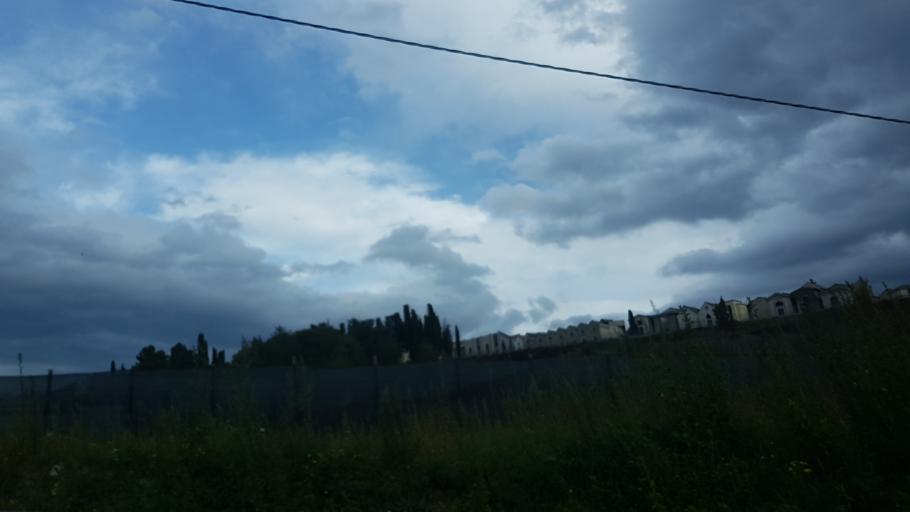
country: IT
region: Abruzzo
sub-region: Provincia dell' Aquila
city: L'Aquila
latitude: 42.3491
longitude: 13.4116
